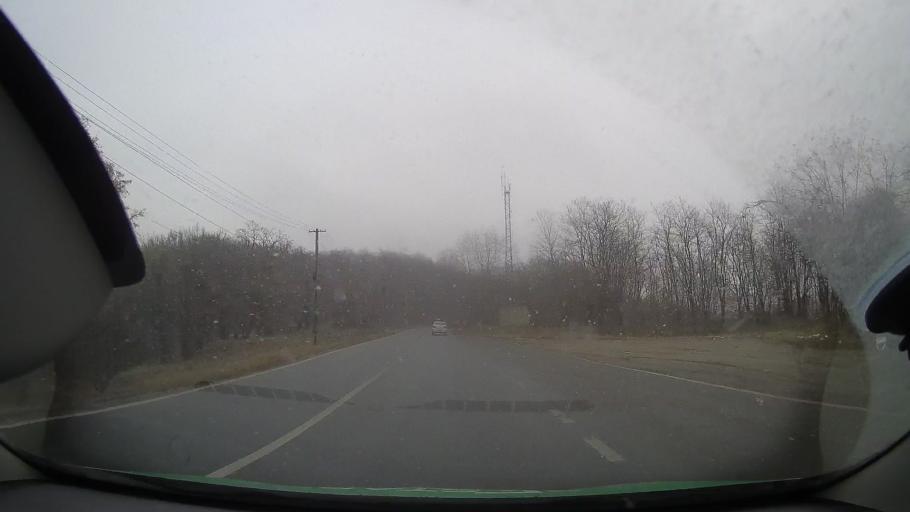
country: RO
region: Sibiu
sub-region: Municipiul Medias
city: Medias
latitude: 46.1841
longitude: 24.3262
